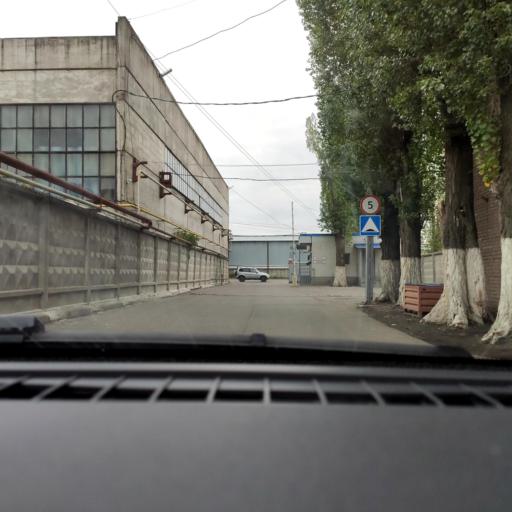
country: RU
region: Voronezj
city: Voronezh
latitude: 51.6554
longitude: 39.2833
